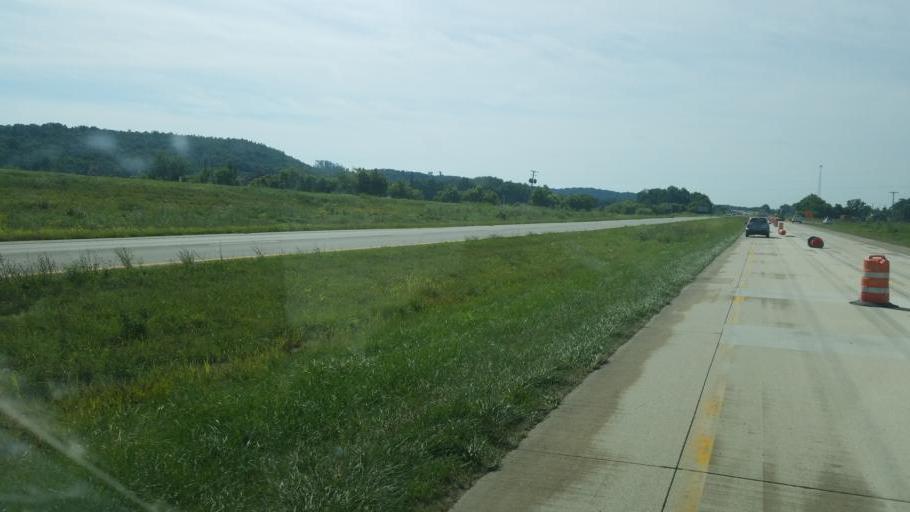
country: US
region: Ohio
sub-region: Hocking County
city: Logan
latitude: 39.4930
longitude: -82.3309
